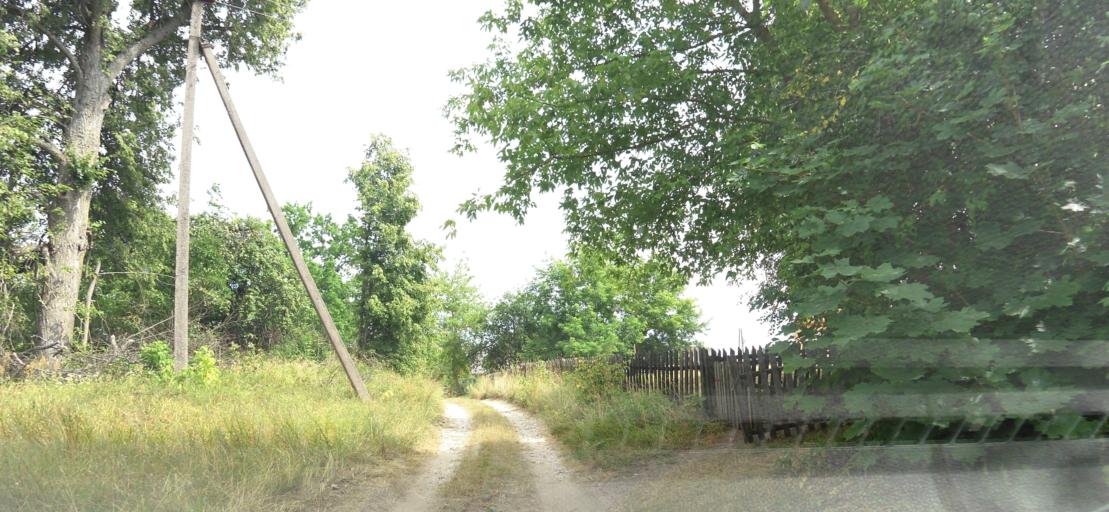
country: LT
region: Alytaus apskritis
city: Druskininkai
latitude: 53.9993
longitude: 24.2894
